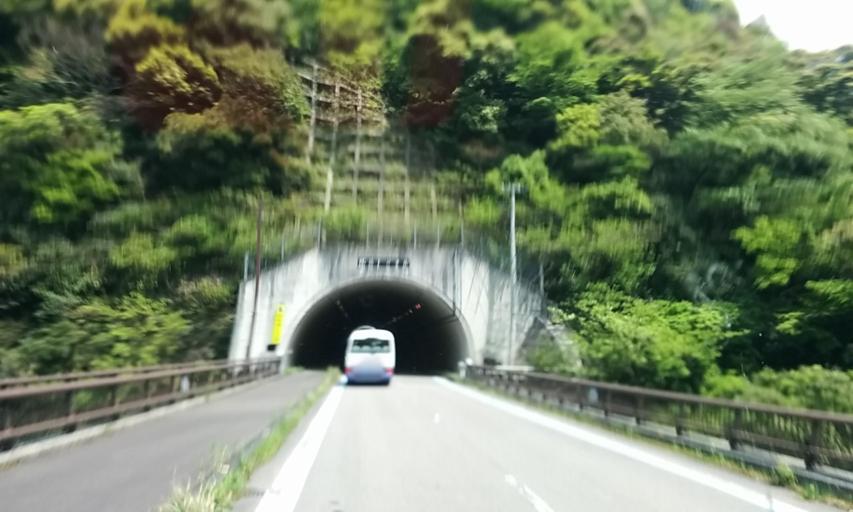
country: JP
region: Ehime
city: Niihama
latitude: 33.8857
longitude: 133.3049
